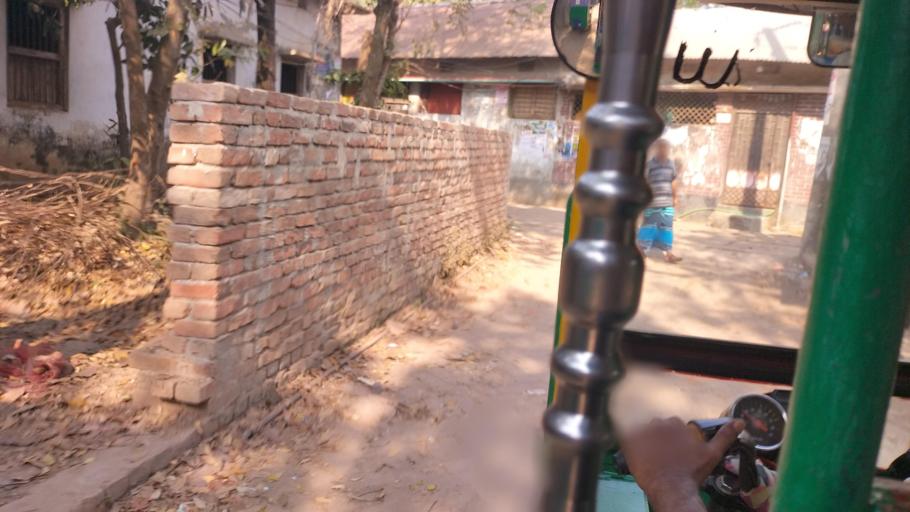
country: BD
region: Dhaka
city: Azimpur
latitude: 23.7946
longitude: 90.3371
